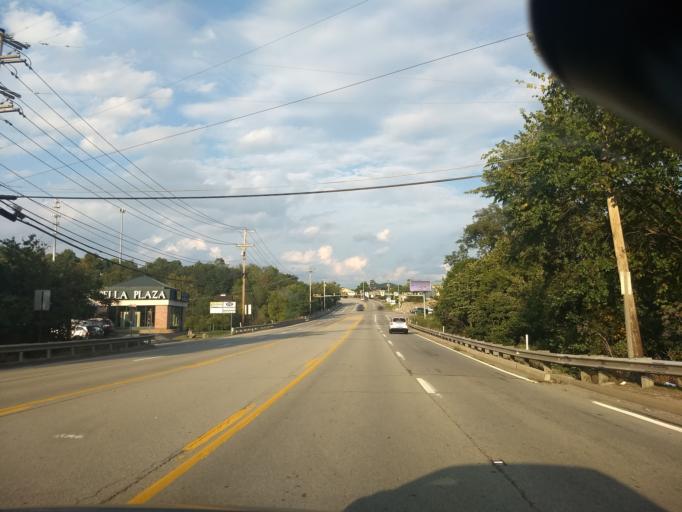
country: US
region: Pennsylvania
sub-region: Washington County
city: Thompsonville
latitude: 40.2910
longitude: -80.1078
